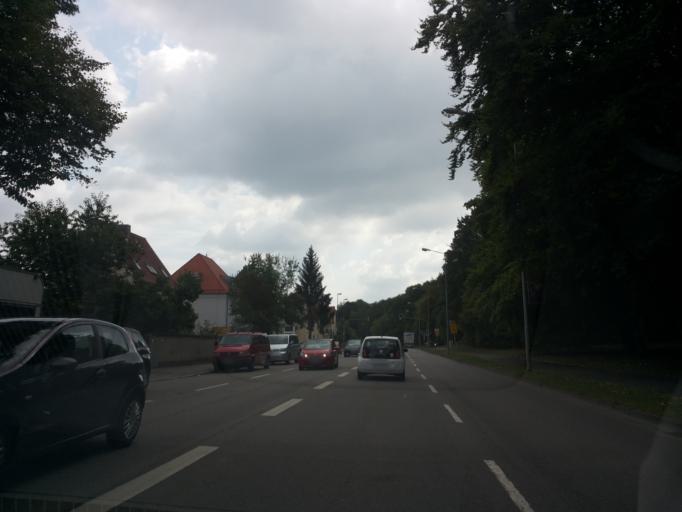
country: DE
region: Bavaria
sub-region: Upper Bavaria
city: Ingolstadt
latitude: 48.7731
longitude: 11.4247
